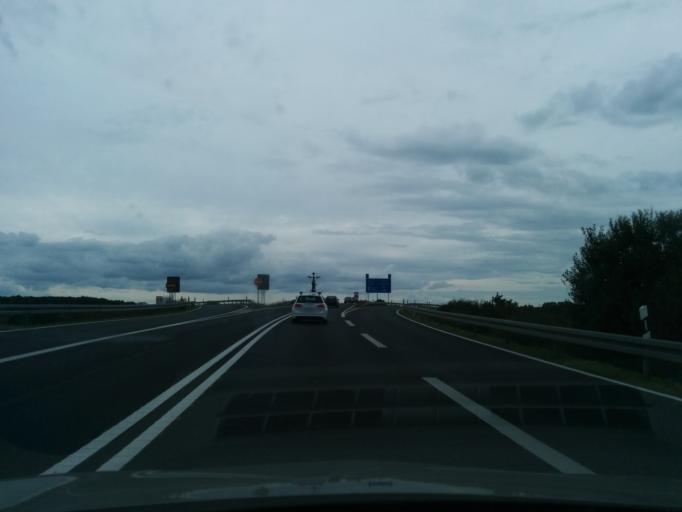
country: DE
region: Mecklenburg-Vorpommern
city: Jarmen
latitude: 53.9474
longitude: 13.3711
